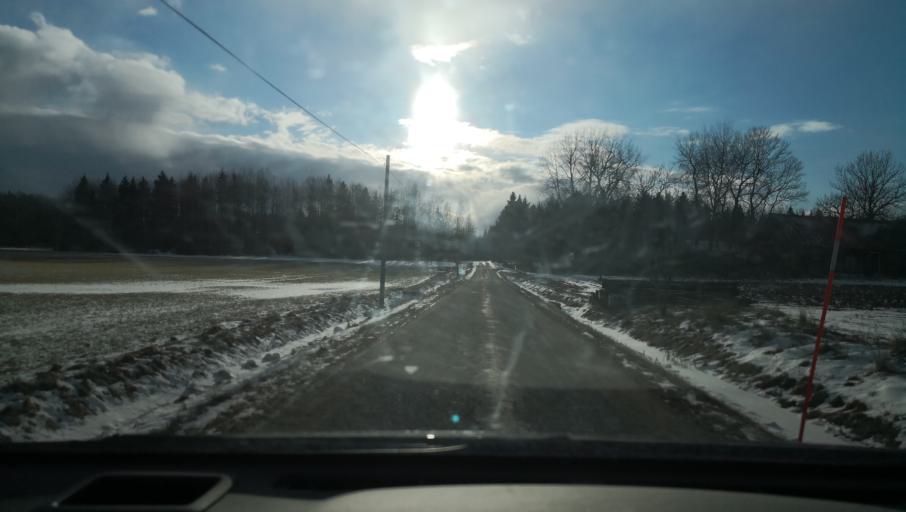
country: SE
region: Uppsala
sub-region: Enkopings Kommun
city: Irsta
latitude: 59.7052
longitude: 16.8778
